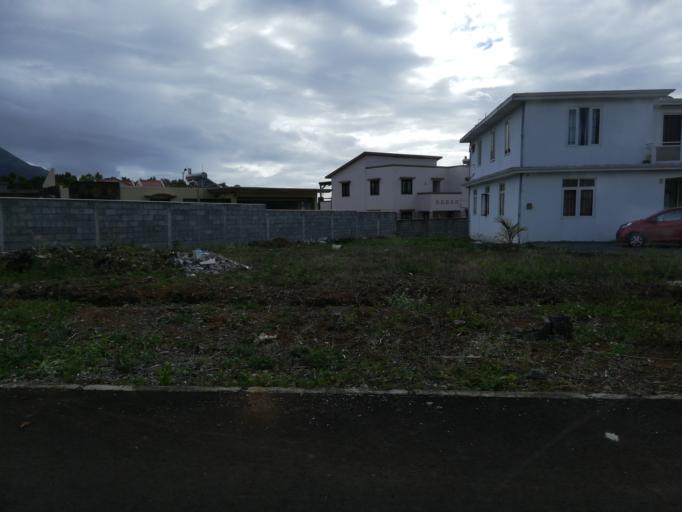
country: MU
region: Plaines Wilhems
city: Ebene
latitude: -20.2471
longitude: 57.4854
